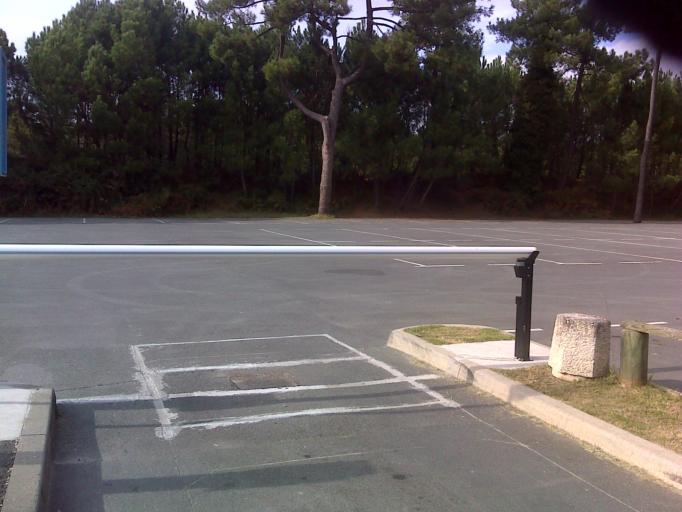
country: FR
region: Poitou-Charentes
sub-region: Departement de la Charente-Maritime
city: Les Mathes
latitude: 45.6919
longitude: -1.1889
